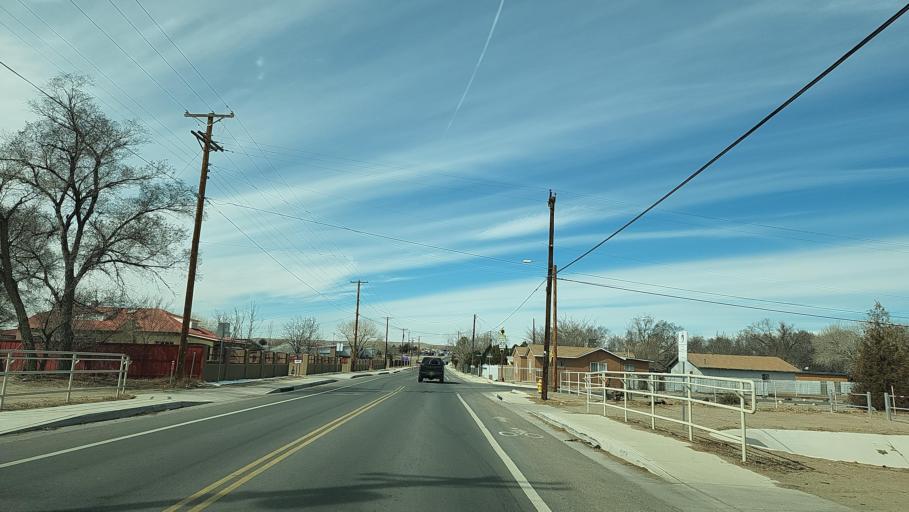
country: US
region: New Mexico
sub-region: Bernalillo County
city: South Valley
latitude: 35.0361
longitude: -106.7076
